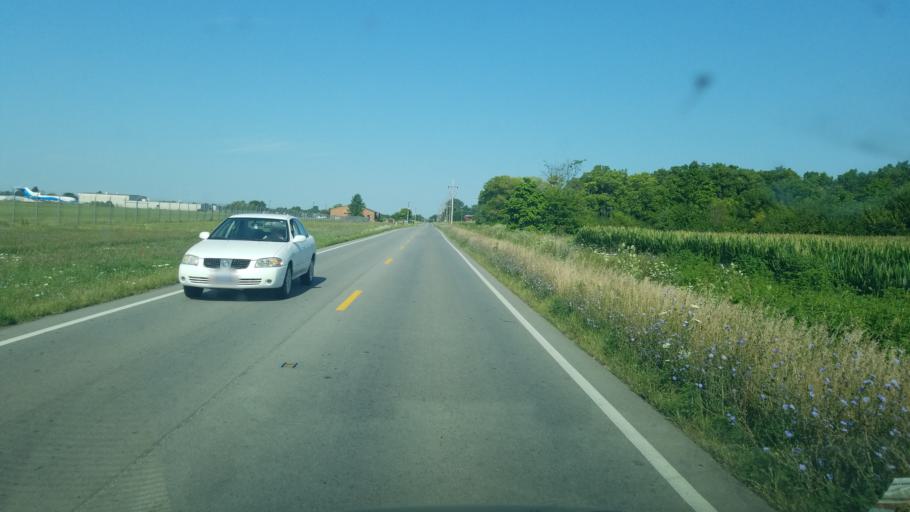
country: US
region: Ohio
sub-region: Franklin County
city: Lincoln Village
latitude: 39.9108
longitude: -83.1304
